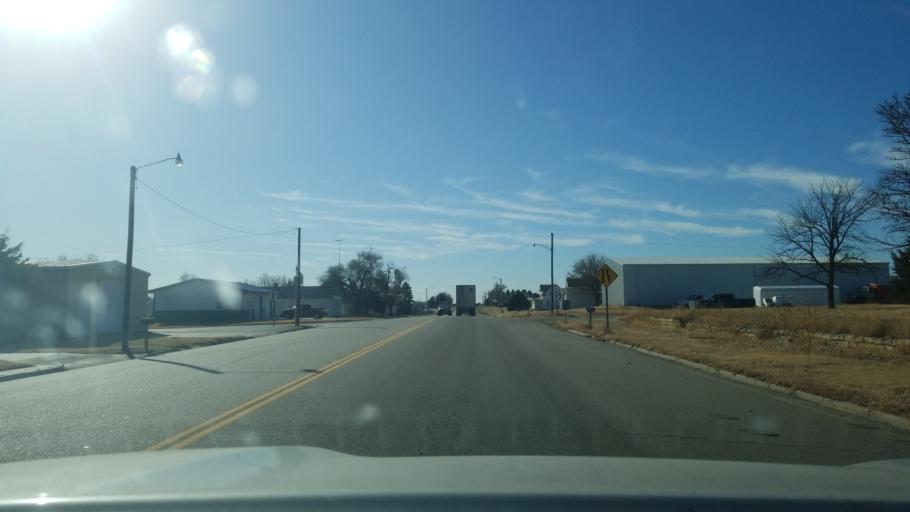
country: US
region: Kansas
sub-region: Ness County
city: Ness City
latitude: 38.4479
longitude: -99.9050
